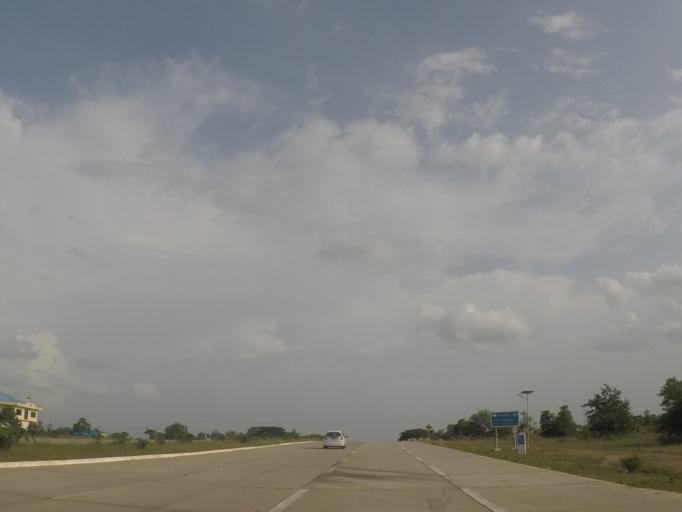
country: MM
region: Mandalay
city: Yamethin
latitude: 20.4990
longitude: 95.8246
